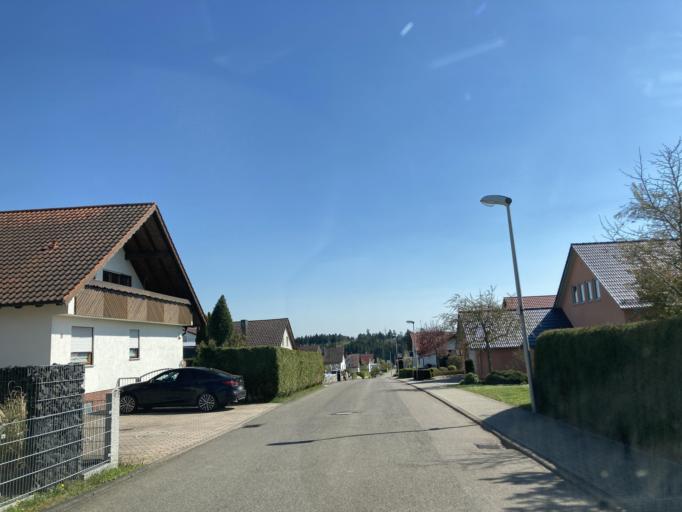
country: DE
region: Baden-Wuerttemberg
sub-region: Regierungsbezirk Stuttgart
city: Motzingen
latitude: 48.5132
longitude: 8.7543
